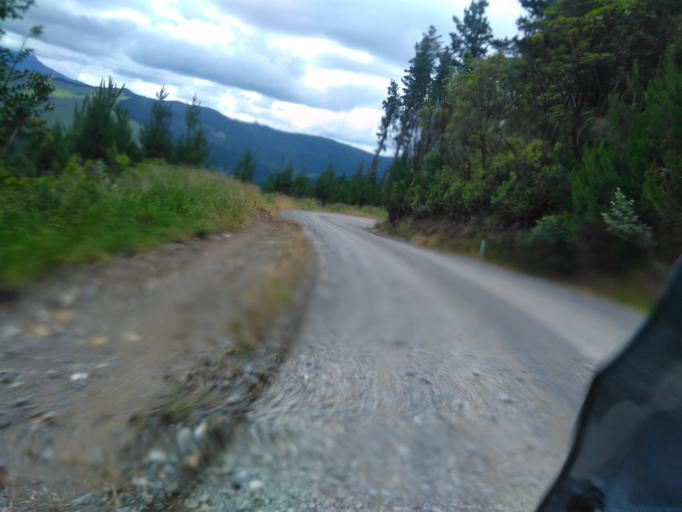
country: NZ
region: Gisborne
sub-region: Gisborne District
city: Gisborne
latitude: -38.0536
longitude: 178.1029
